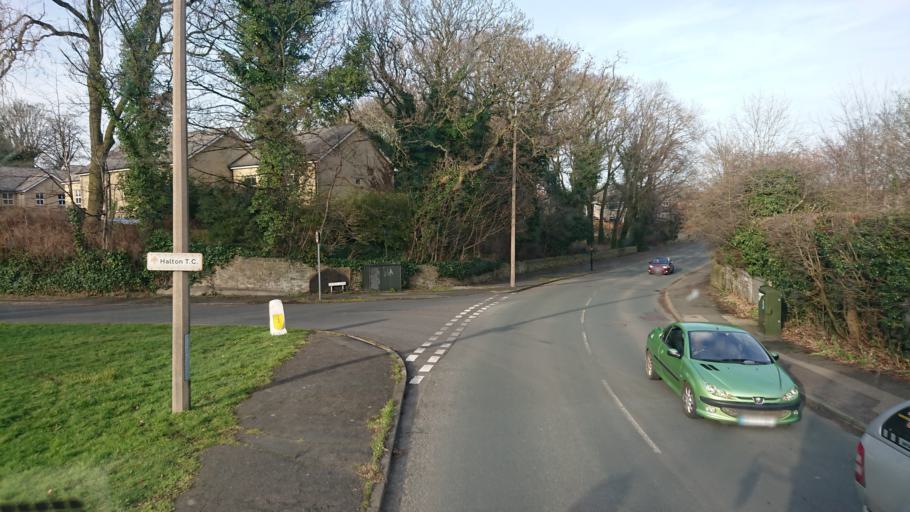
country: GB
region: England
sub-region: Lancashire
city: Bolton le Sands
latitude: 54.0667
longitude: -2.7947
